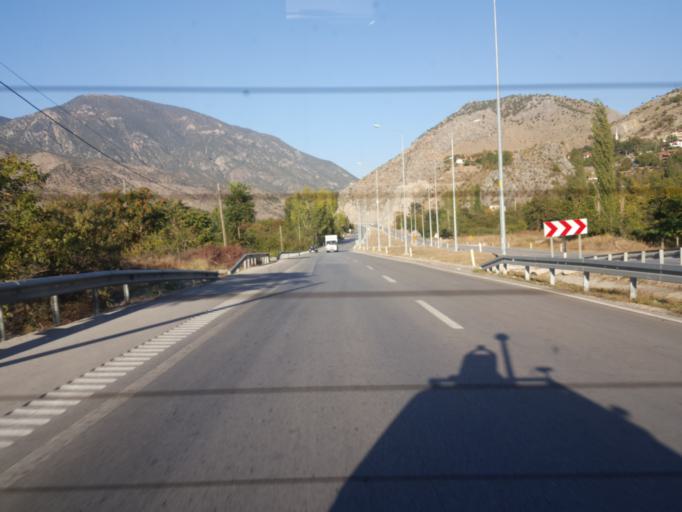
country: TR
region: Amasya
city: Amasya
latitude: 40.6762
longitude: 35.8736
